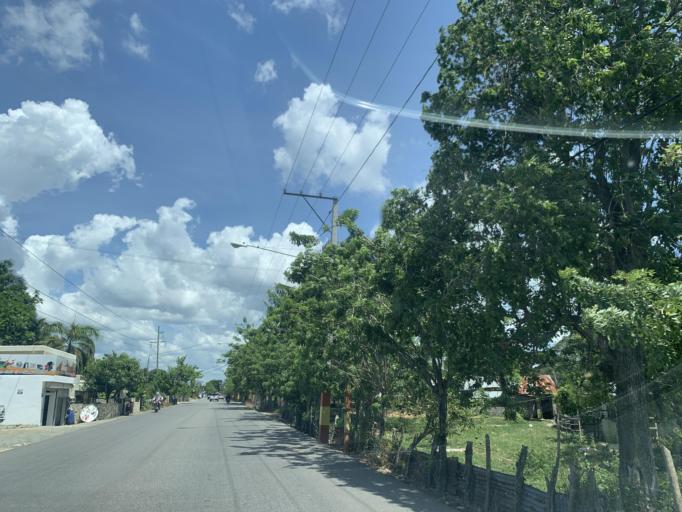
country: DO
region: Puerto Plata
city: Cabarete
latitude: 19.6895
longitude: -70.3789
